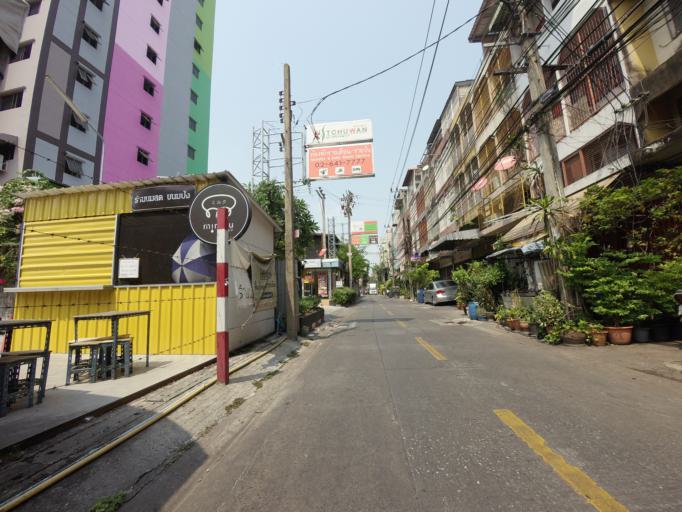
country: TH
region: Bangkok
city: Din Daeng
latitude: 13.7620
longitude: 100.5601
